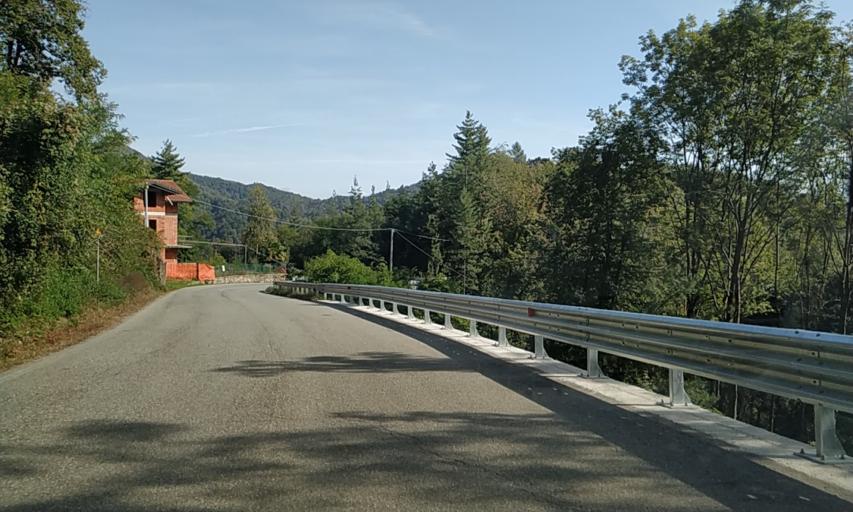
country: IT
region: Piedmont
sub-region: Provincia di Biella
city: Coggiola
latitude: 45.6784
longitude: 8.1806
